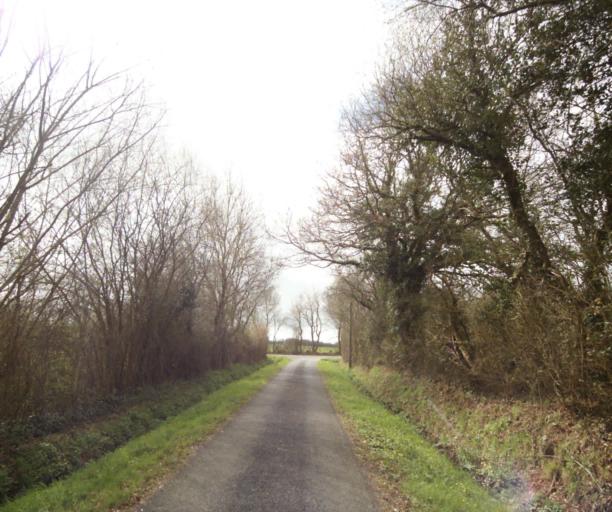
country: FR
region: Pays de la Loire
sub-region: Departement de la Loire-Atlantique
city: Bouvron
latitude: 47.4237
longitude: -1.8948
